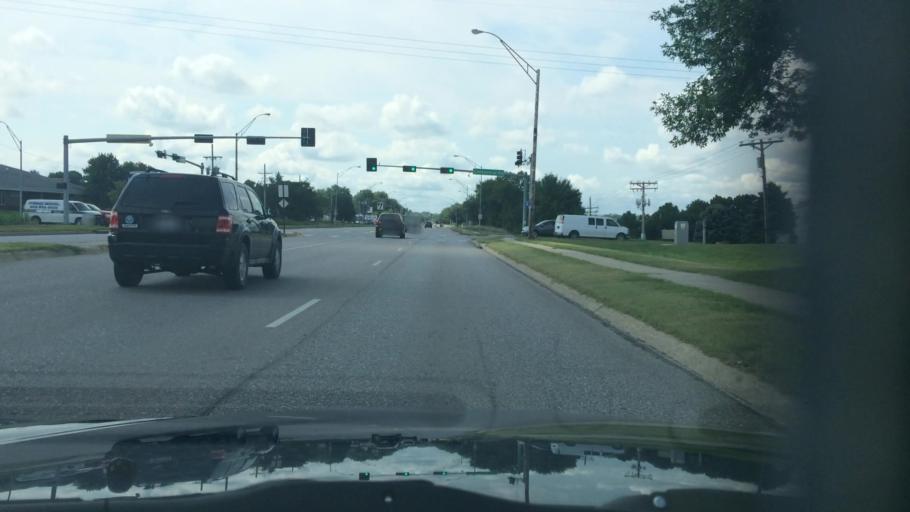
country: US
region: Nebraska
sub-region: Sarpy County
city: Papillion
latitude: 41.1695
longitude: -96.0432
